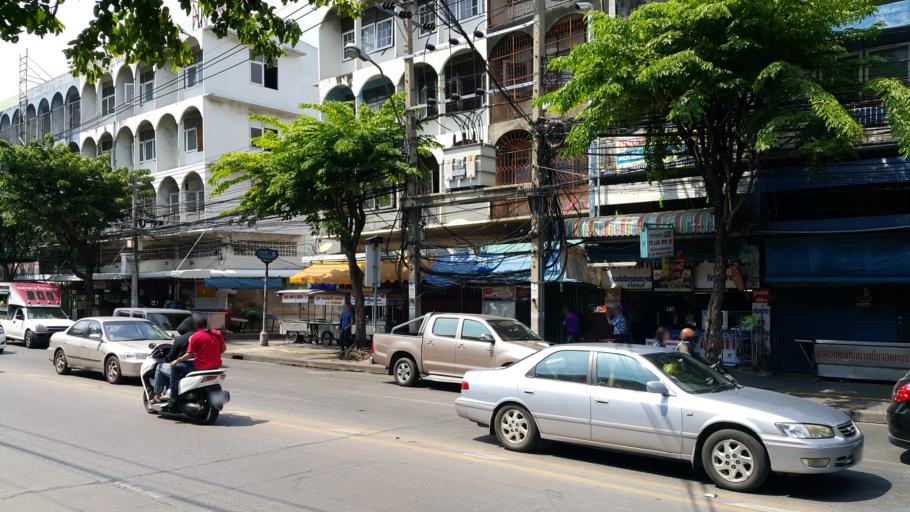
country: TH
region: Bangkok
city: Phra Khanong
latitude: 13.7115
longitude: 100.6097
